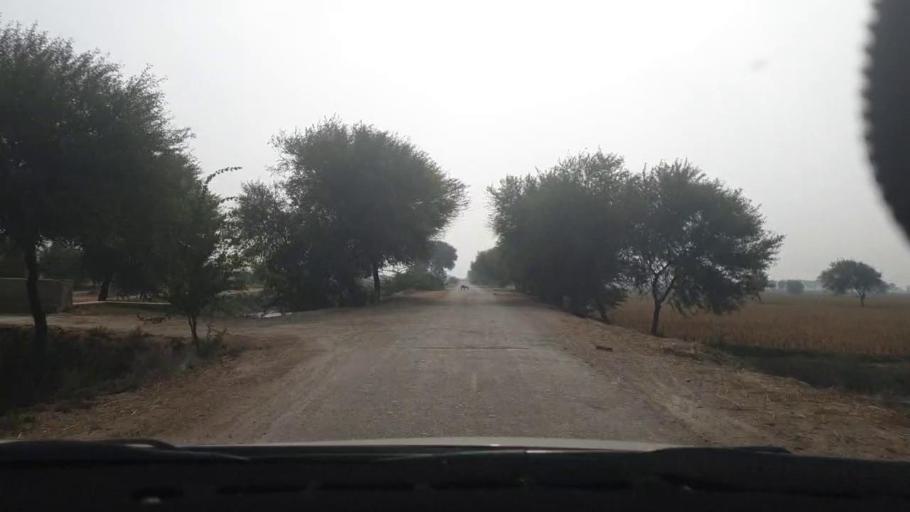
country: PK
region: Sindh
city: Tando Muhammad Khan
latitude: 25.0649
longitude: 68.5413
